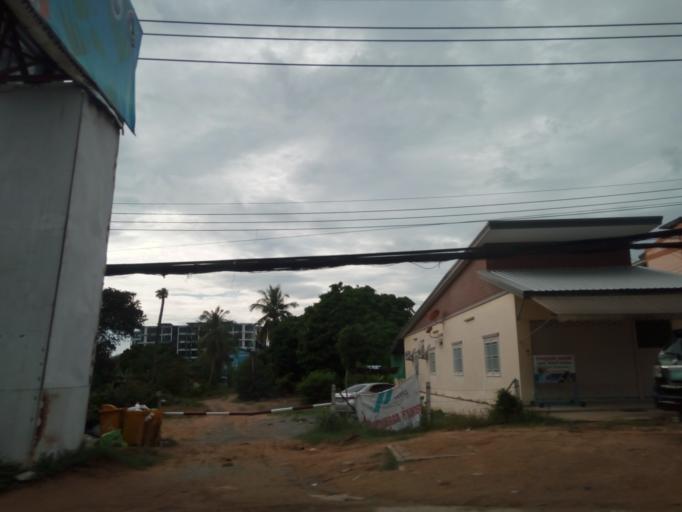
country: TH
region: Phuket
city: Thalang
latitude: 8.0976
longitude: 98.3063
